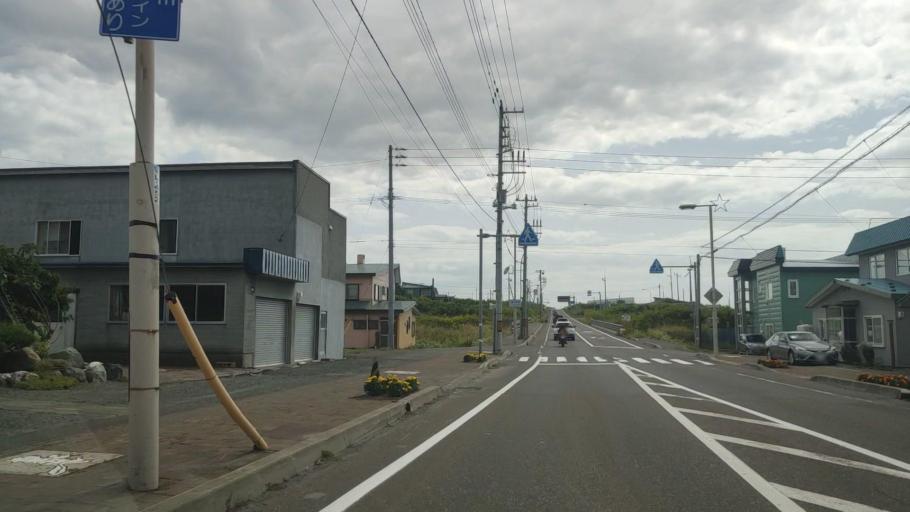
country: JP
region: Hokkaido
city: Rumoi
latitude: 44.5312
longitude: 141.7666
